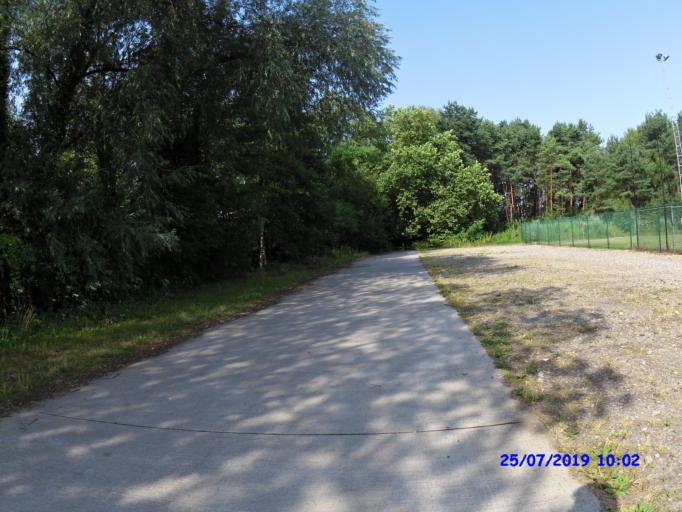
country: BE
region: Flanders
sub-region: Provincie Antwerpen
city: Balen
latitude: 51.1974
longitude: 5.2212
